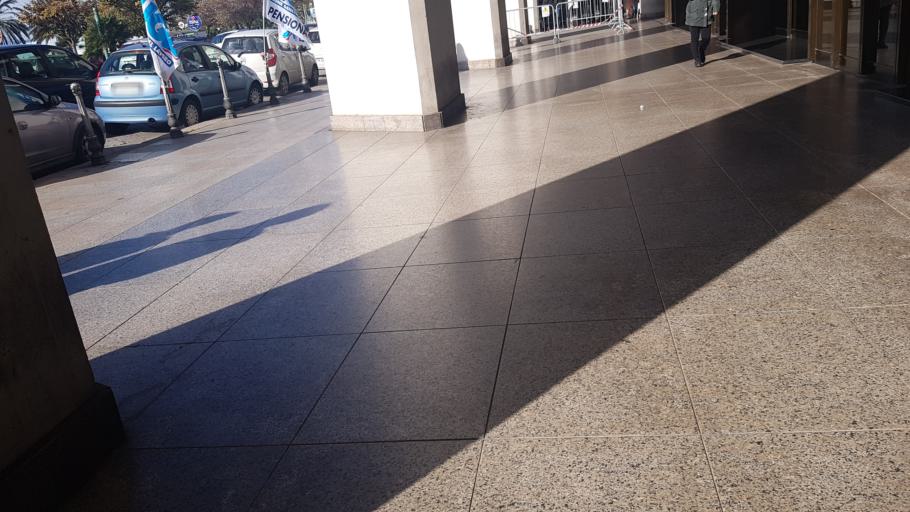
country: IT
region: Sardinia
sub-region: Provincia di Cagliari
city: Cagliari
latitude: 39.2129
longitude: 9.1146
